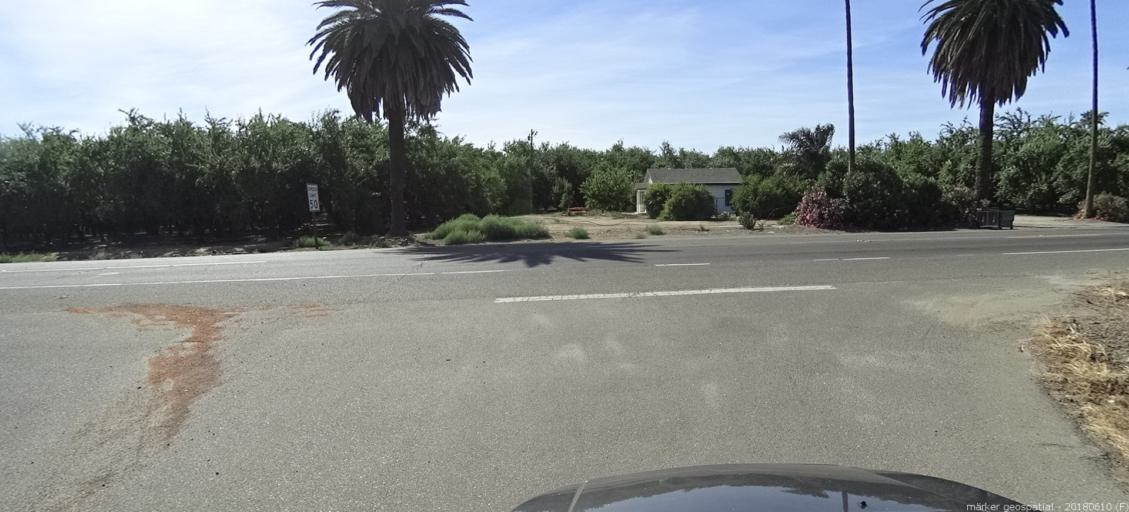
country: US
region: California
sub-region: Madera County
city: Chowchilla
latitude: 37.1021
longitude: -120.2817
